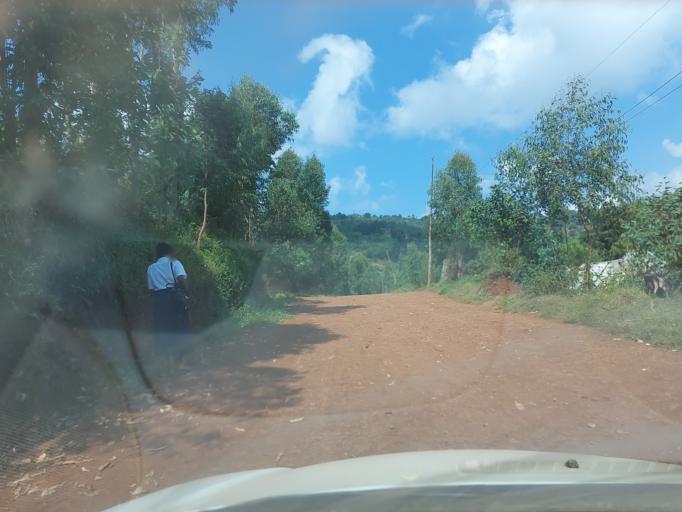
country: CD
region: South Kivu
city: Bukavu
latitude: -2.5065
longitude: 28.8272
